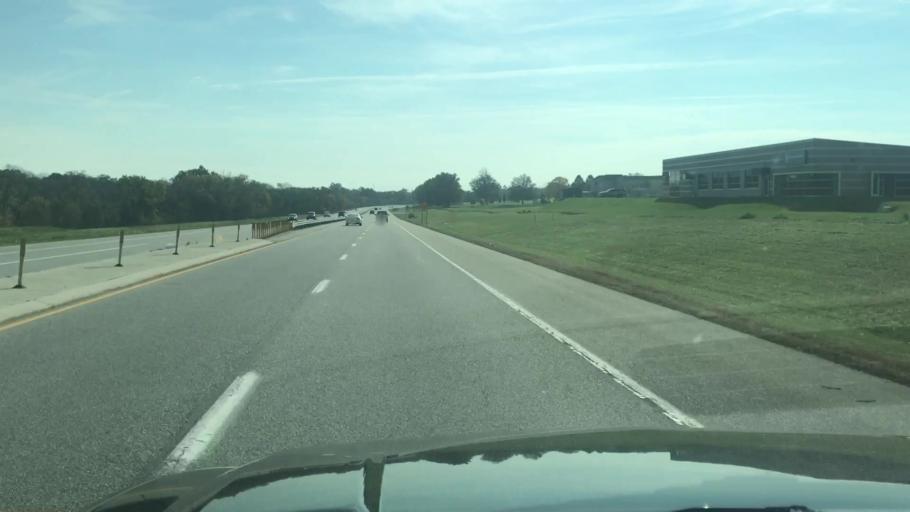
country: US
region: Pennsylvania
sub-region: Cumberland County
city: Mechanicsburg
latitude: 40.2616
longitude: -77.0397
